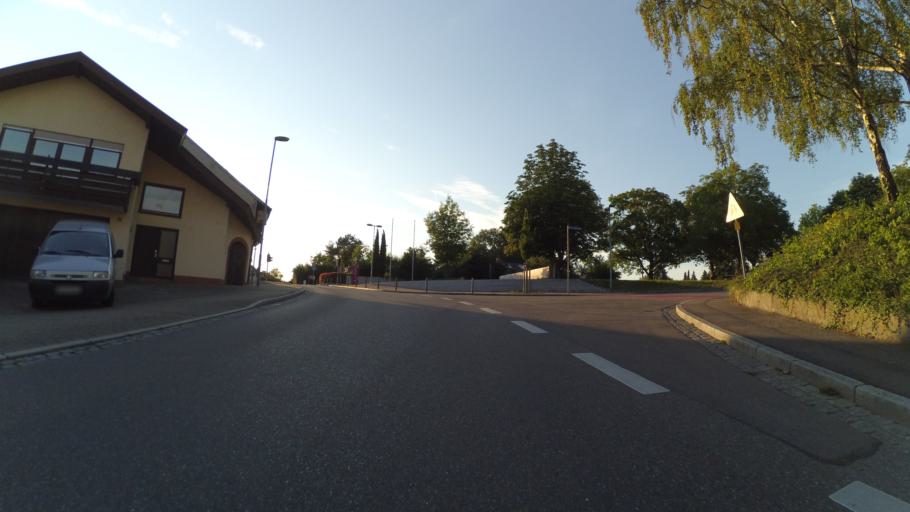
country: DE
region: Baden-Wuerttemberg
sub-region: Freiburg Region
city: Heitersheim
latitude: 47.8721
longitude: 7.6647
